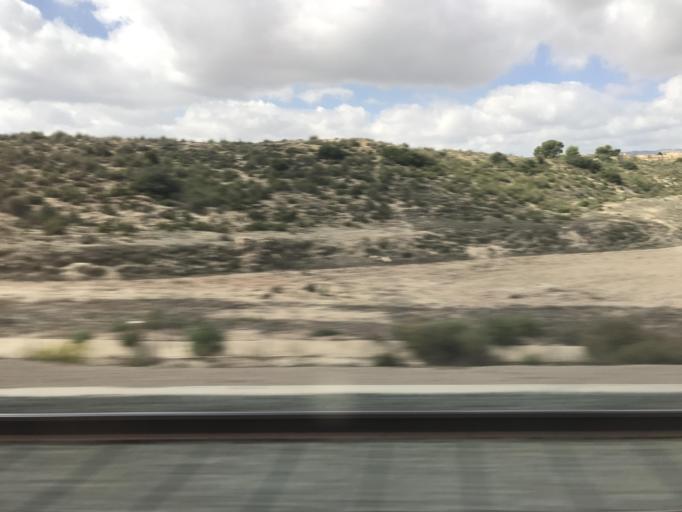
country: ES
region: Castille-La Mancha
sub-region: Provincia de Albacete
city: Caudete
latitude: 38.7157
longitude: -0.9315
